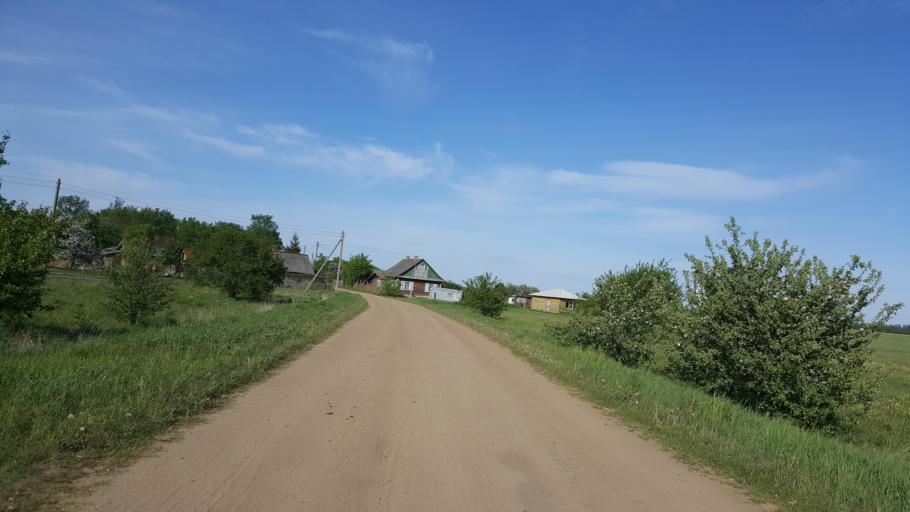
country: BY
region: Brest
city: Kamyanyets
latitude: 52.3603
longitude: 23.8657
